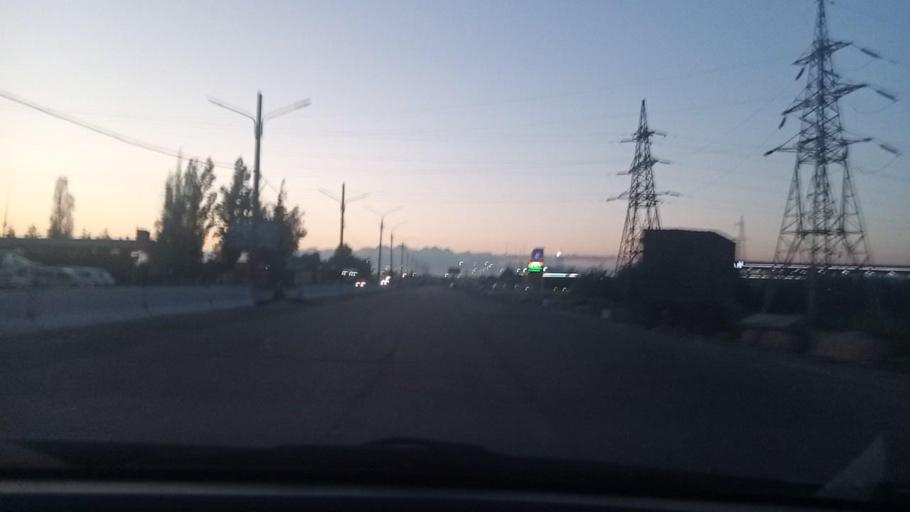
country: UZ
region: Toshkent Shahri
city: Tashkent
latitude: 41.2440
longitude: 69.2308
